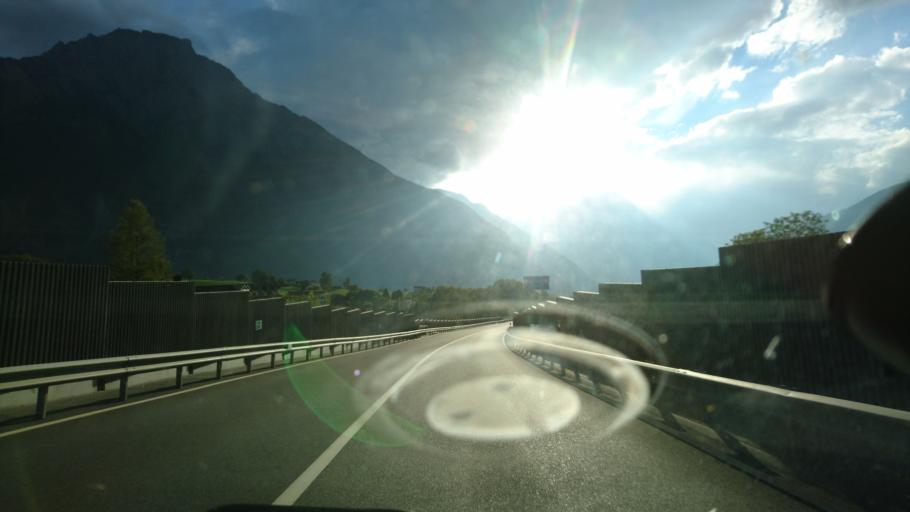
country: CH
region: Valais
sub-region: Brig District
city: Naters
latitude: 46.3174
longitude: 8.0150
